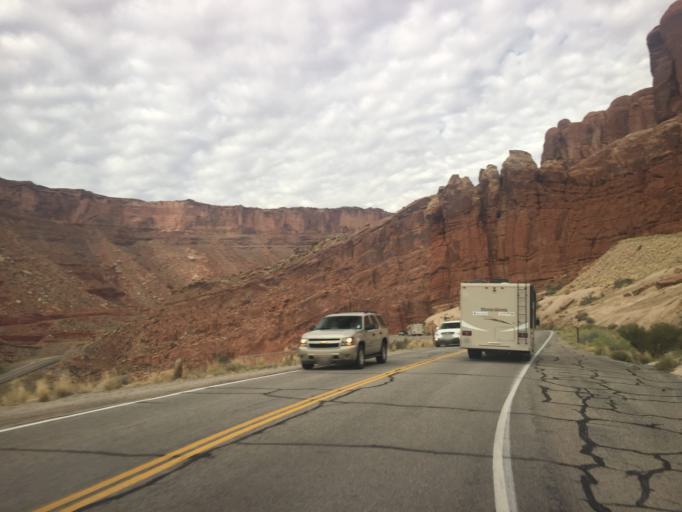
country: US
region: Utah
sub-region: Grand County
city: Moab
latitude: 38.6187
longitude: -109.6157
